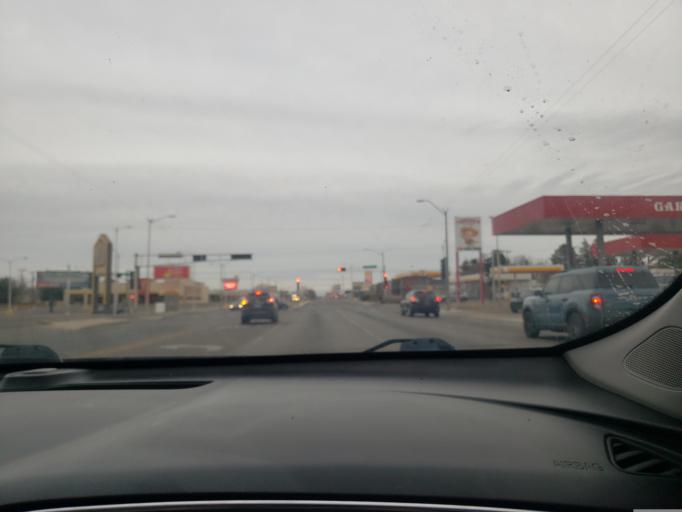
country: US
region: New Mexico
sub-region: Bernalillo County
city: North Valley
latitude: 35.1159
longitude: -106.5863
